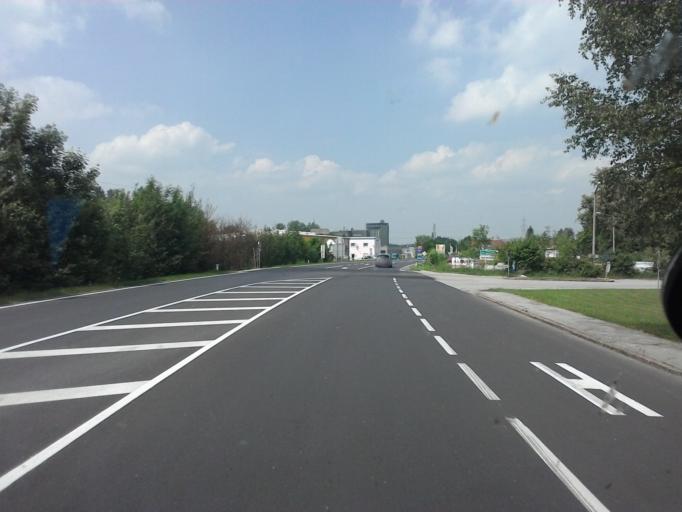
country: AT
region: Upper Austria
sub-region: Wels-Land
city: Sattledt
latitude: 48.0766
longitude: 14.0465
